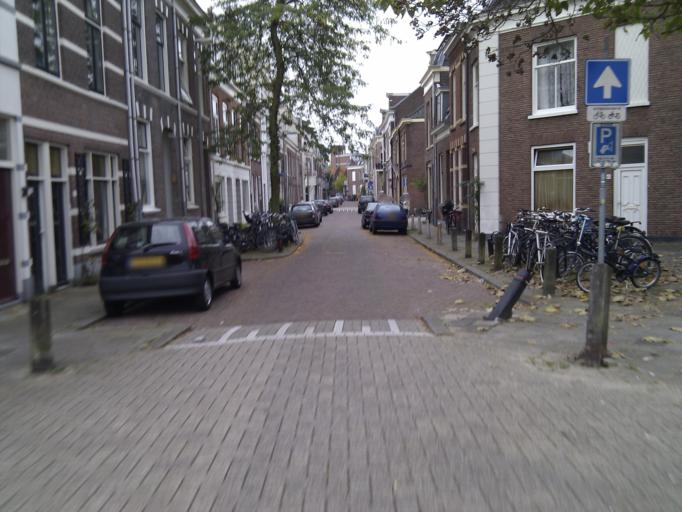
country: NL
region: Utrecht
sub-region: Gemeente Utrecht
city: Utrecht
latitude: 52.0970
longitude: 5.1362
